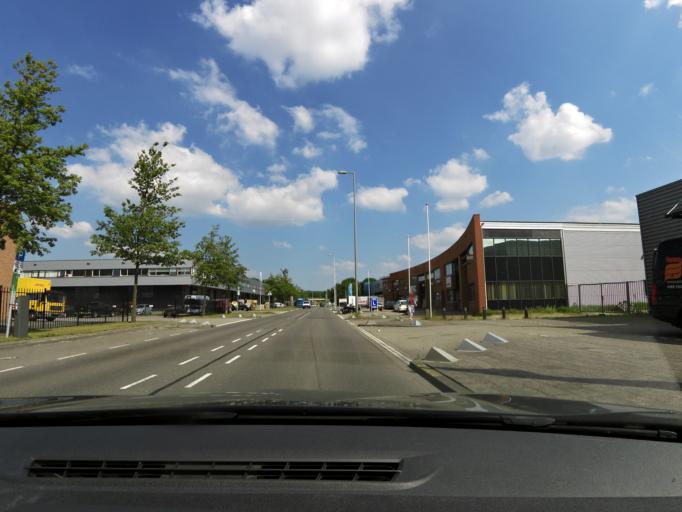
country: NL
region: South Holland
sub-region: Gemeente Albrandswaard
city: Rhoon
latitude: 51.8673
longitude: 4.3772
